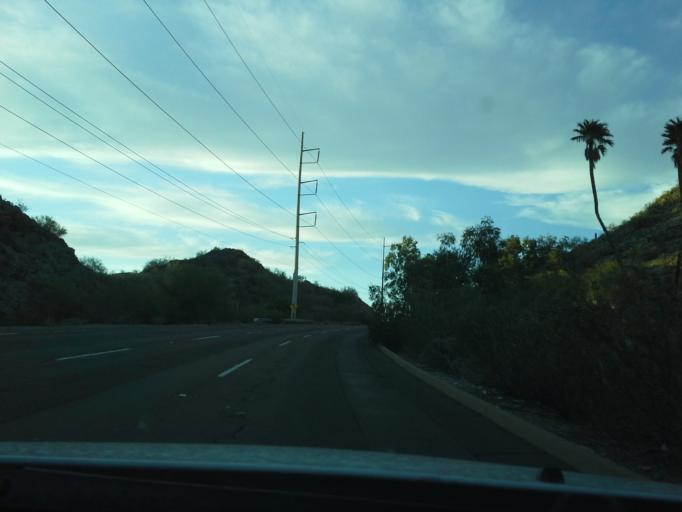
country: US
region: Arizona
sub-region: Maricopa County
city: Glendale
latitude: 33.5898
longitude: -112.0650
